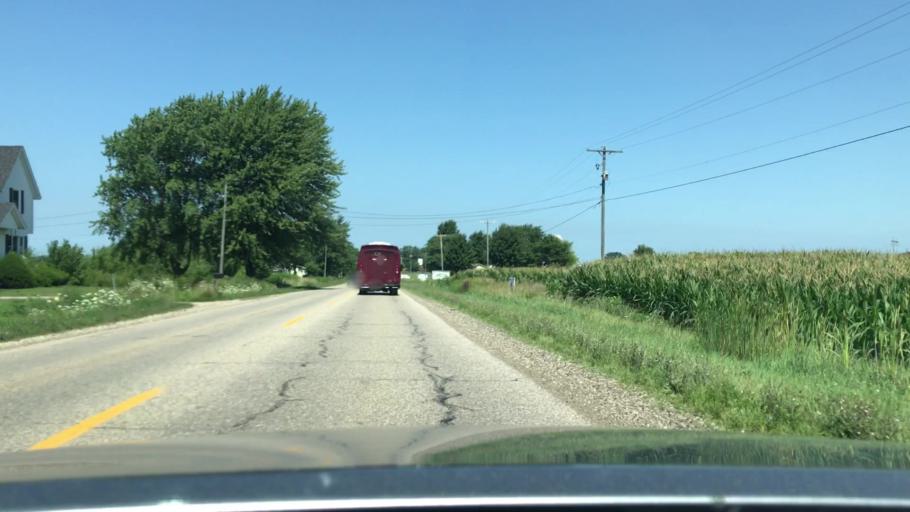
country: US
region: Michigan
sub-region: Ottawa County
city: Zeeland
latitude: 42.8733
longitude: -86.0799
